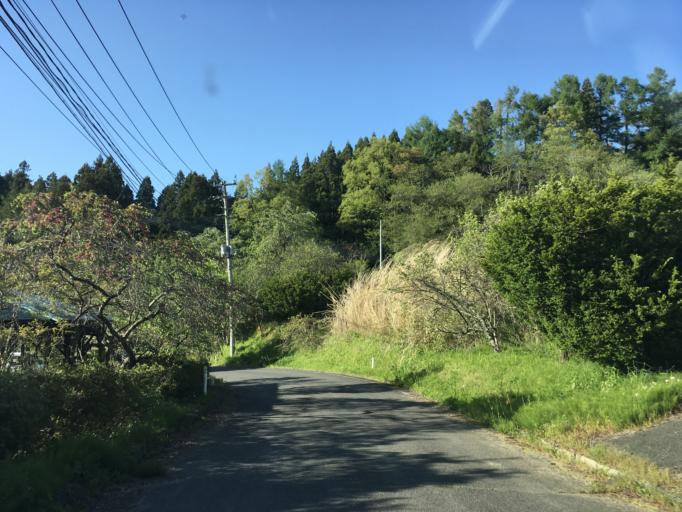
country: JP
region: Iwate
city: Ichinoseki
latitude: 38.8605
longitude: 141.3334
